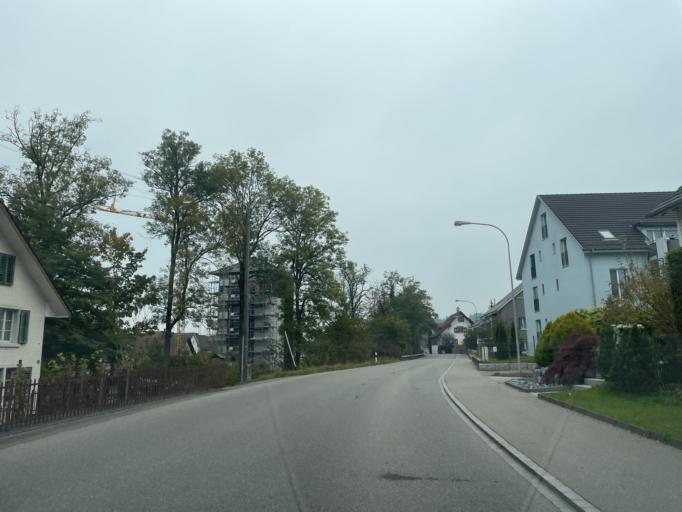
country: CH
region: Zurich
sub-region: Bezirk Winterthur
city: Neftenbach / Dorf Neftenbach
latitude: 47.5263
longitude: 8.6615
